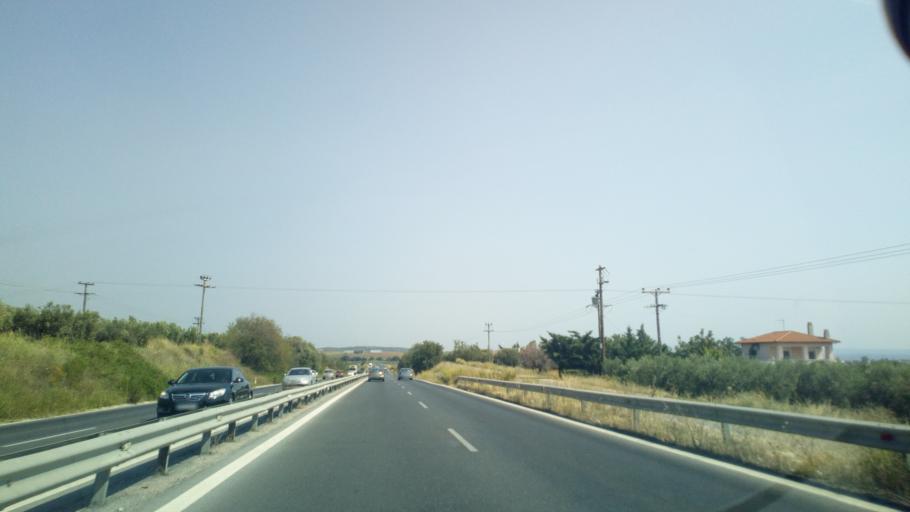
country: GR
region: Central Macedonia
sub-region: Nomos Chalkidikis
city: Nea Flogita
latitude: 40.2691
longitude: 23.2251
